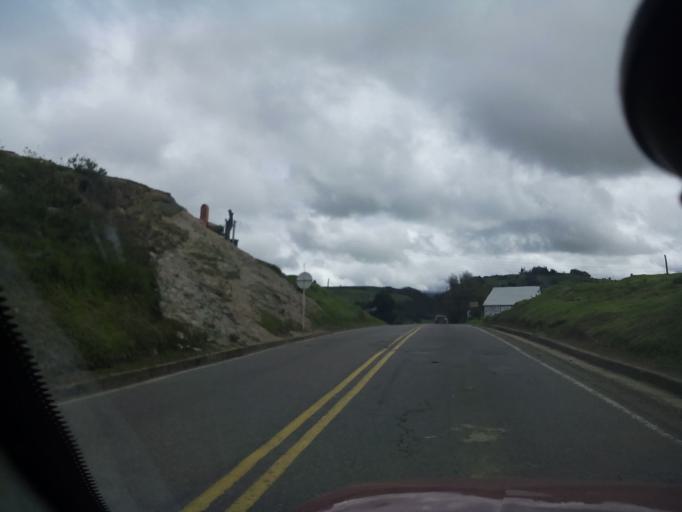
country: CO
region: Boyaca
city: Combita
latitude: 5.6524
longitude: -73.3532
